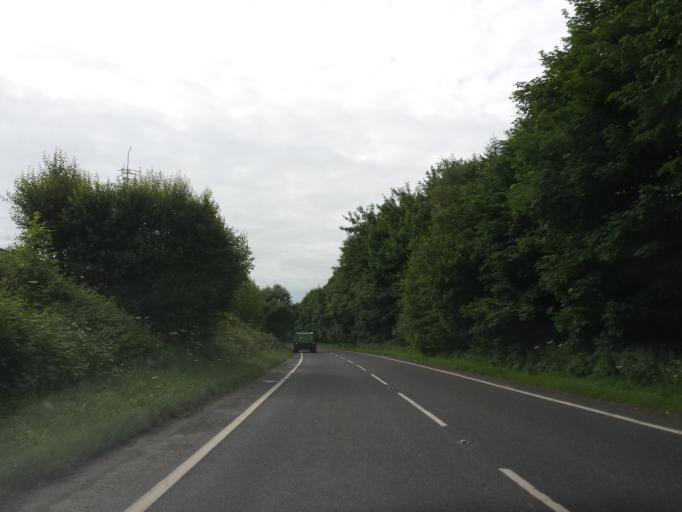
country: GB
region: Scotland
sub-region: Dumfries and Galloway
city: Moffat
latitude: 55.3204
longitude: -3.4673
